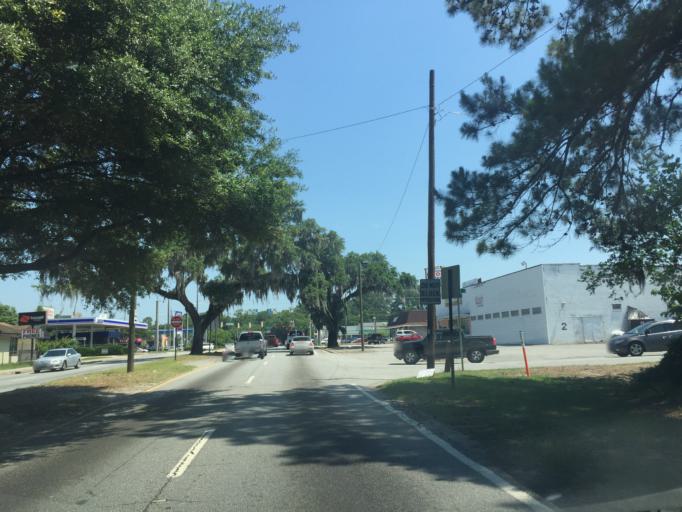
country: US
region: Georgia
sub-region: Chatham County
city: Savannah
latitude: 32.0275
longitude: -81.1113
